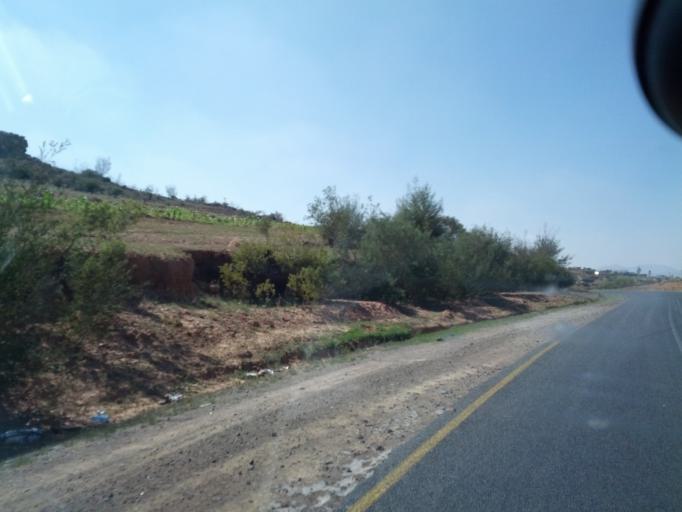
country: LS
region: Berea
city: Teyateyaneng
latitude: -29.1421
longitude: 27.7121
